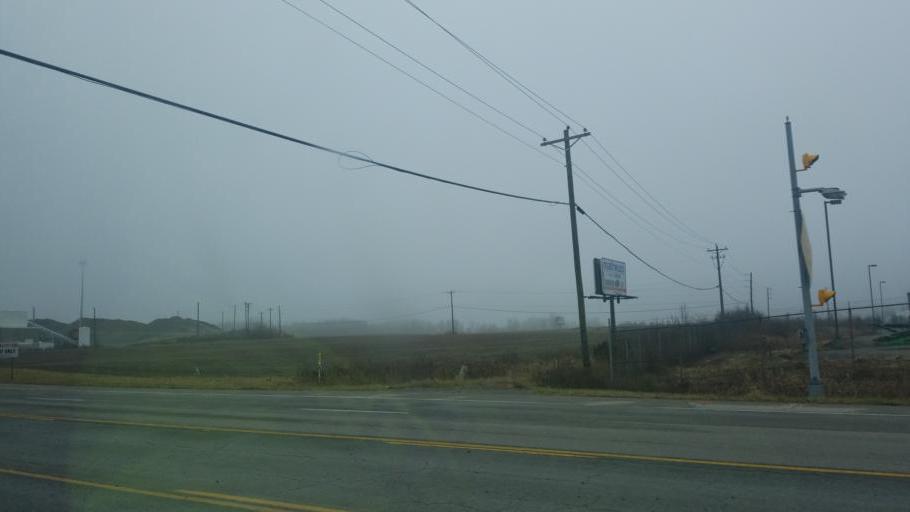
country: US
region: Ohio
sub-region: Champaign County
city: North Lewisburg
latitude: 40.2763
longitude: -83.5165
